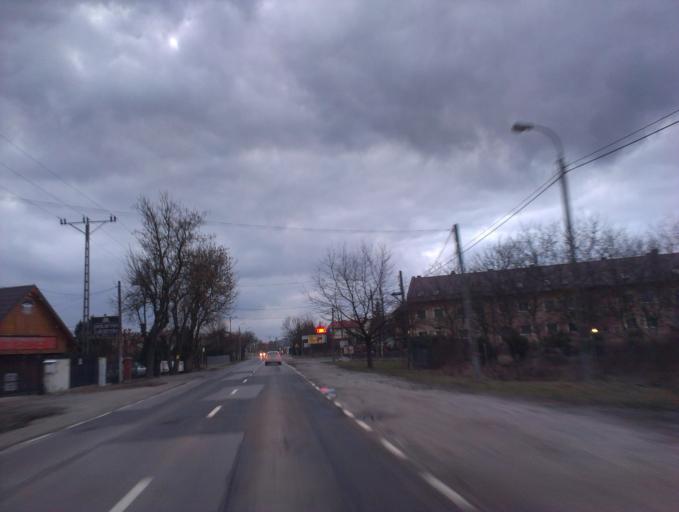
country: PL
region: Masovian Voivodeship
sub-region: Powiat piaseczynski
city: Konstancin-Jeziorna
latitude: 52.0852
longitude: 21.0918
